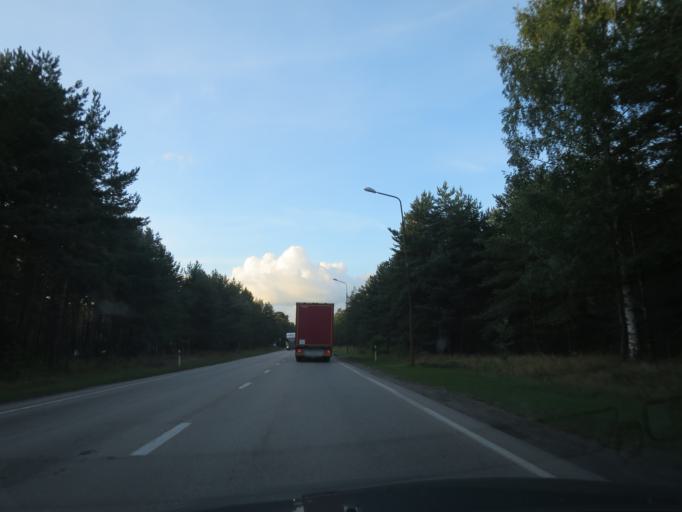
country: LV
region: Salacgrivas
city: Salacgriva
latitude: 57.7649
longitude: 24.3562
